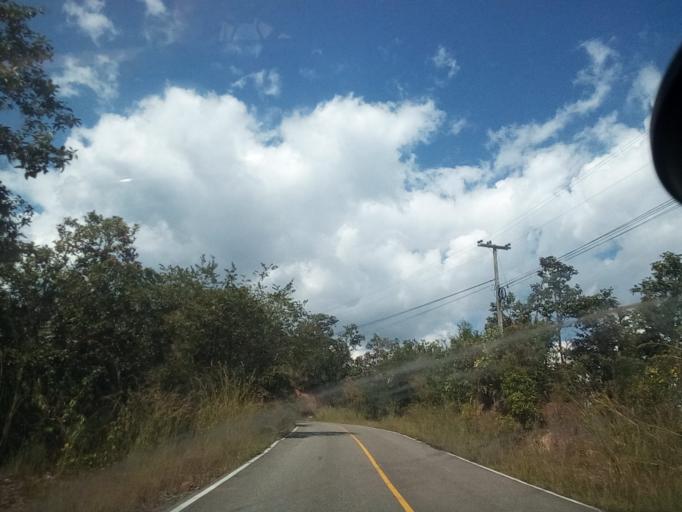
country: TH
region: Chiang Mai
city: Samoeng
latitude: 18.8711
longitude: 98.6905
